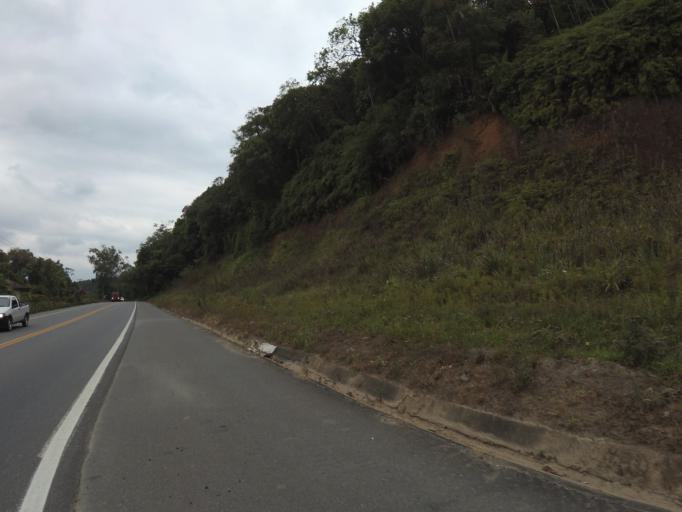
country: BR
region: Santa Catarina
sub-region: Indaial
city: Indaial
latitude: -26.8371
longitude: -49.1651
